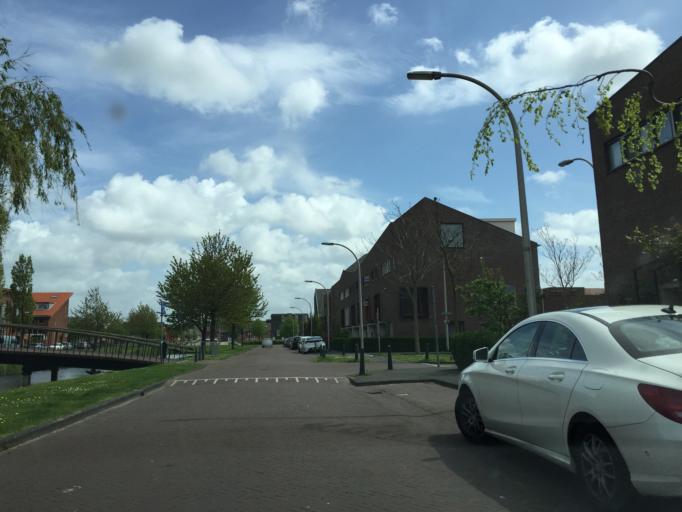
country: NL
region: South Holland
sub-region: Gemeente Den Haag
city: Ypenburg
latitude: 52.0361
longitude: 4.3610
